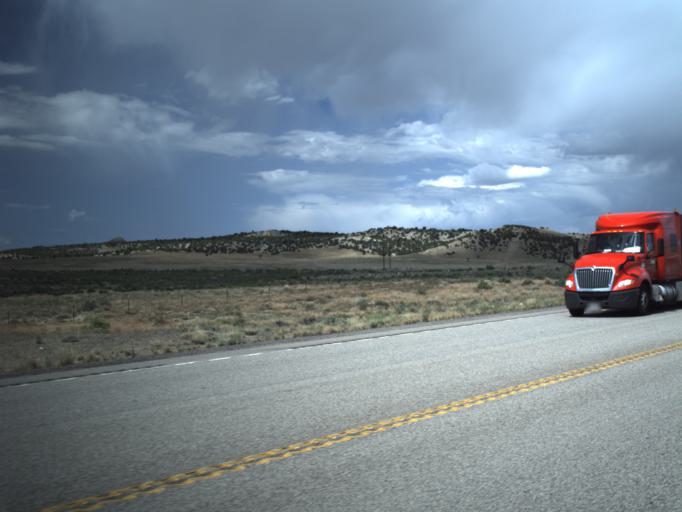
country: US
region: Utah
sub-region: Carbon County
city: Wellington
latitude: 39.5425
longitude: -110.6121
